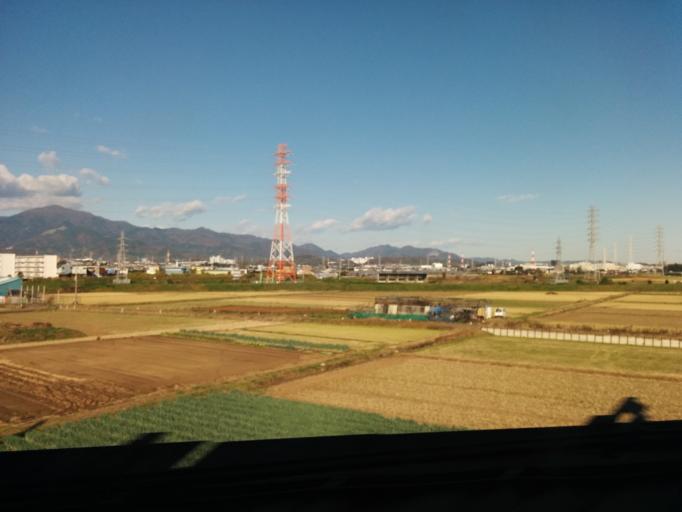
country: JP
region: Kanagawa
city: Isehara
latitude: 35.3768
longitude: 139.3498
